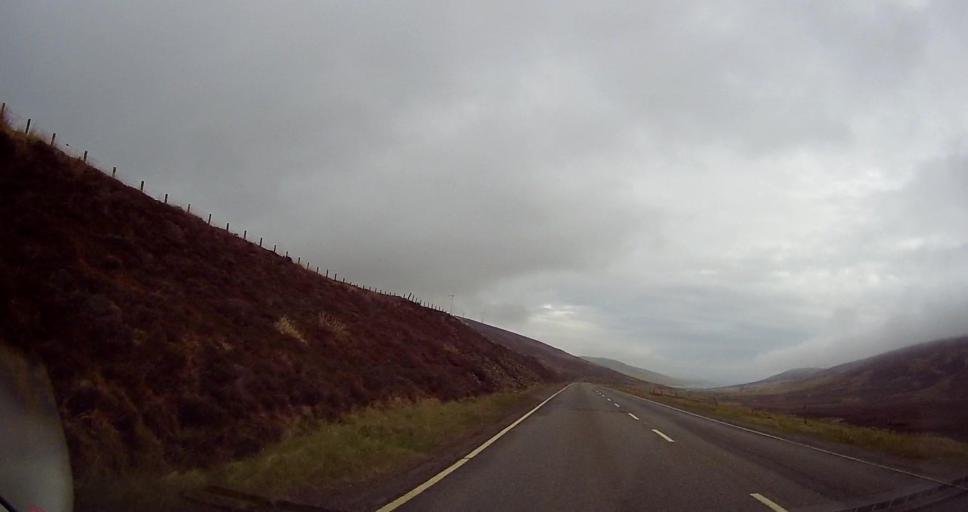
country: GB
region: Scotland
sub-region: Shetland Islands
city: Lerwick
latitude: 60.1492
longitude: -1.2383
